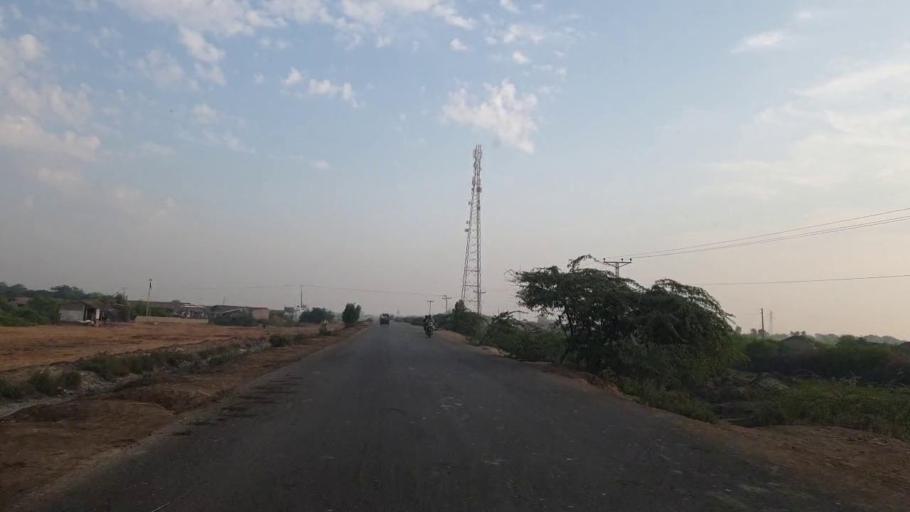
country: PK
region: Sindh
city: Badin
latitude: 24.6975
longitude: 68.9209
